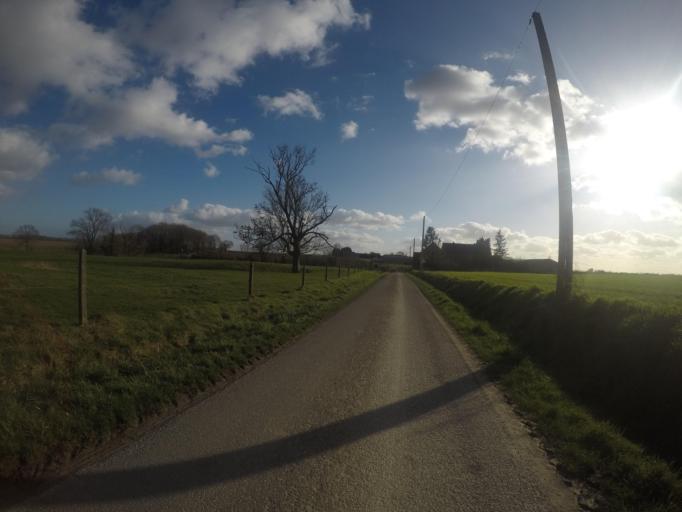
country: BE
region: Wallonia
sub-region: Province du Hainaut
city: Enghien
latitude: 50.6526
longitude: 4.0509
